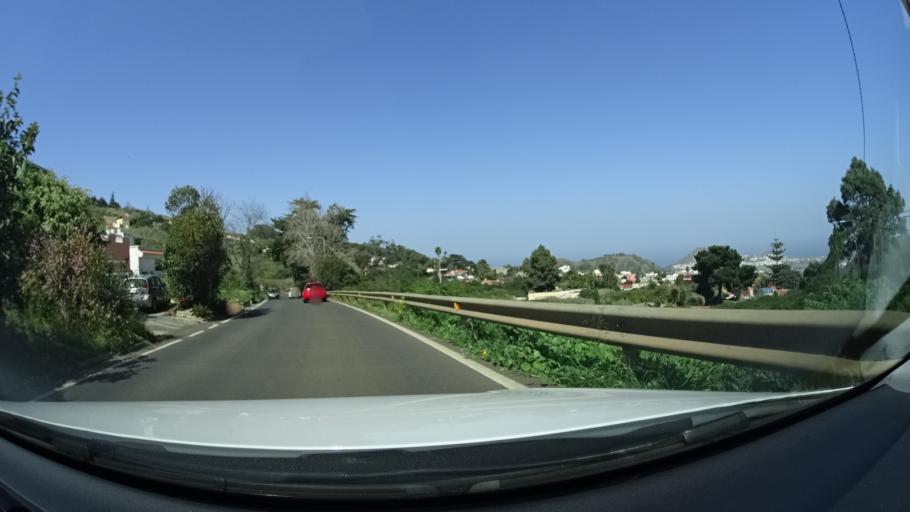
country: ES
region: Canary Islands
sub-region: Provincia de Las Palmas
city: Arucas
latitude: 28.0901
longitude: -15.5355
